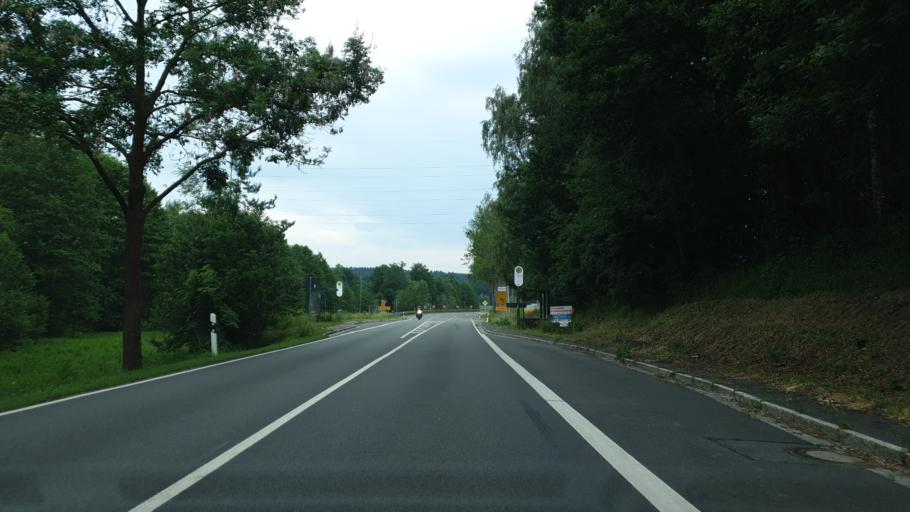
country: DE
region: Saxony
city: Waldkirchen
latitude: 50.5937
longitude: 12.3997
